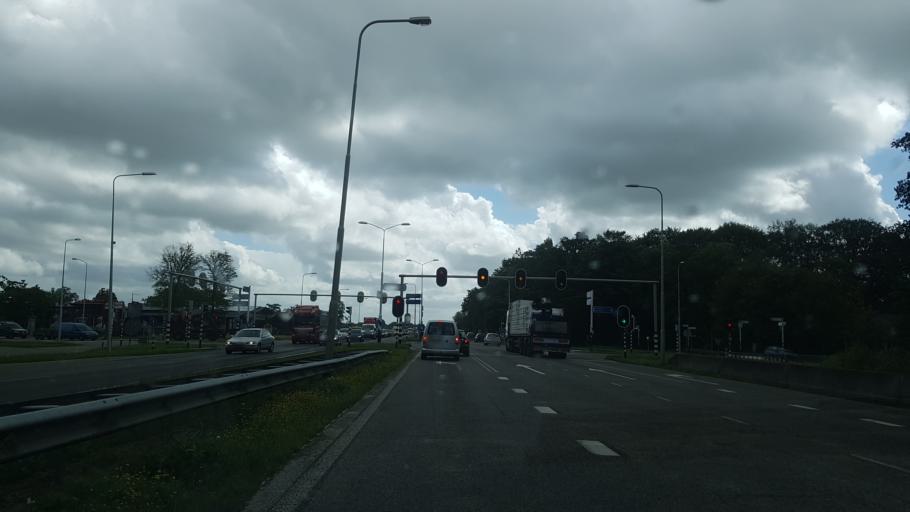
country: NL
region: Friesland
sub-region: Gemeente Tytsjerksteradiel
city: Tytsjerk
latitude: 53.2180
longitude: 5.9076
